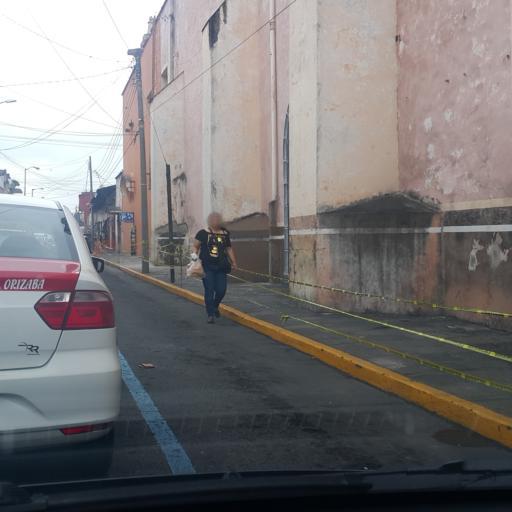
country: MX
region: Veracruz
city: Orizaba
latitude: 18.8446
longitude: -97.1080
